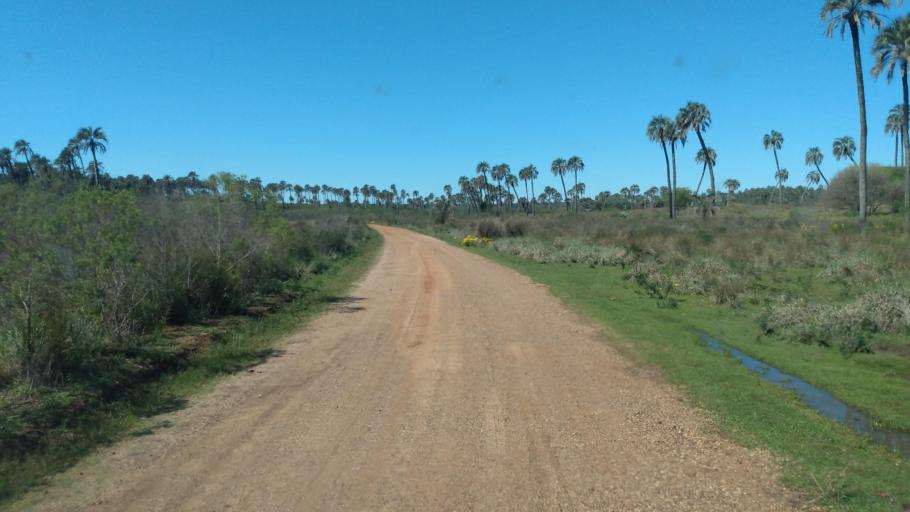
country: AR
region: Entre Rios
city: Ubajay
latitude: -31.8822
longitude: -58.2366
